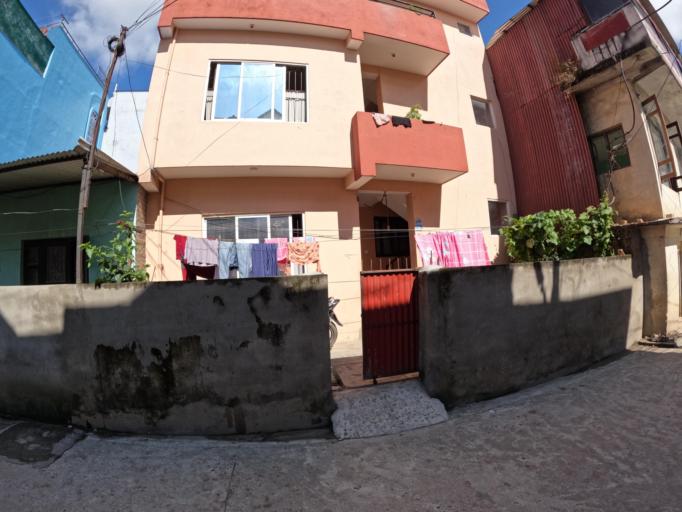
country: NP
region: Central Region
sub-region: Bagmati Zone
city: Kathmandu
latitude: 27.7495
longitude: 85.3362
